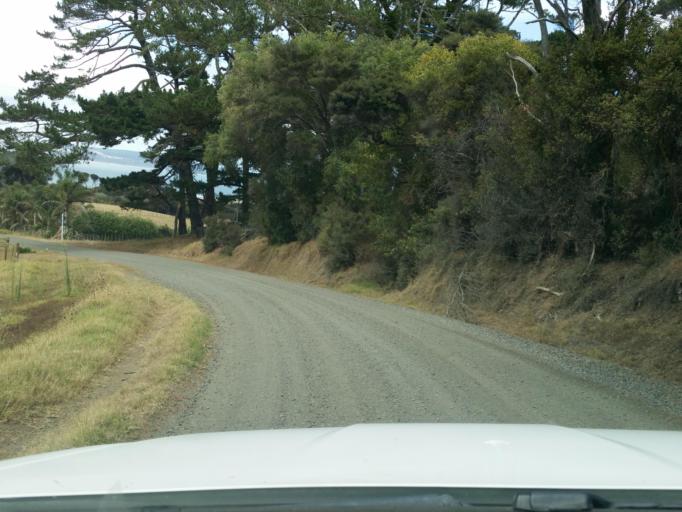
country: NZ
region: Auckland
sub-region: Auckland
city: Wellsford
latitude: -36.3620
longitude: 174.1777
